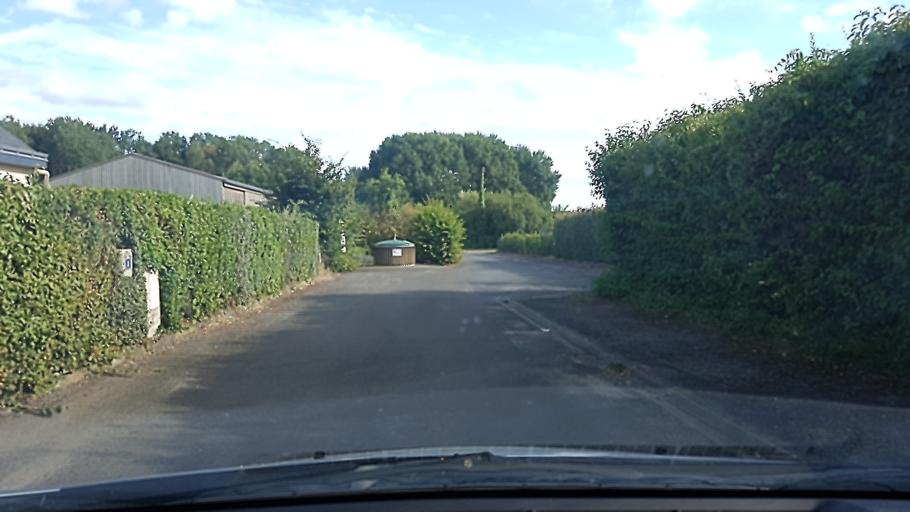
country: FR
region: Pays de la Loire
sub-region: Departement de Maine-et-Loire
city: Jarze
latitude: 47.5238
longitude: -0.2106
